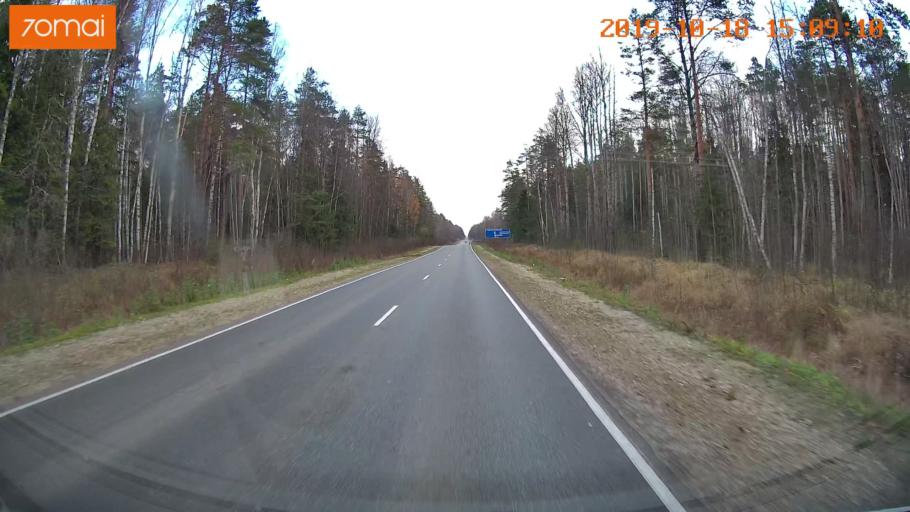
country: RU
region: Vladimir
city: Gus'-Khrustal'nyy
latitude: 55.5625
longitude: 40.6183
